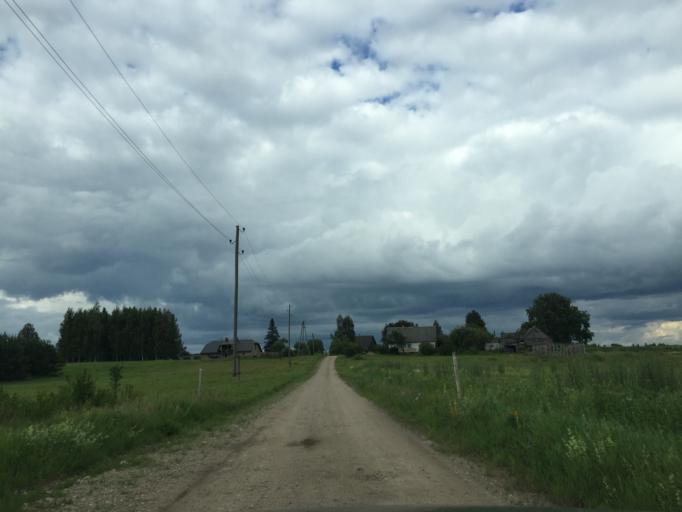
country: LV
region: Malpils
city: Malpils
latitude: 56.9912
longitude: 24.9661
